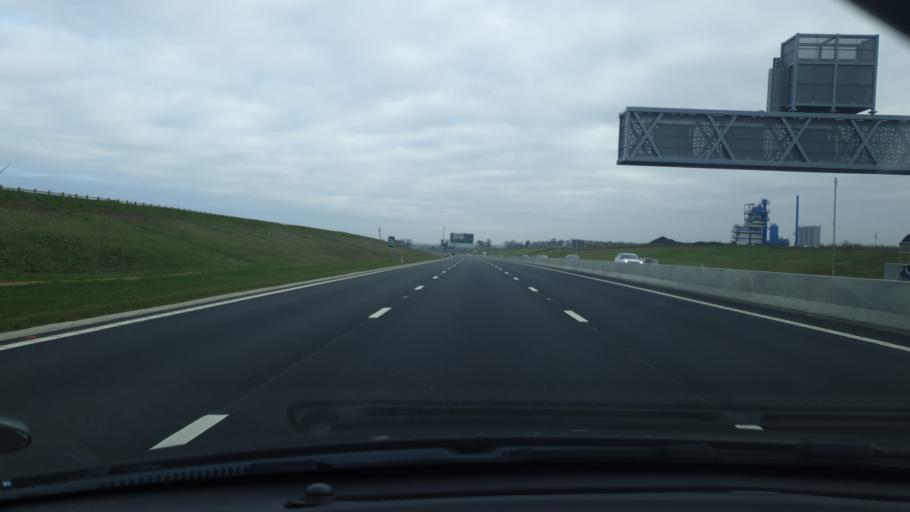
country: GB
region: England
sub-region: Cambridgeshire
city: Godmanchester
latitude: 52.2938
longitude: -0.1637
